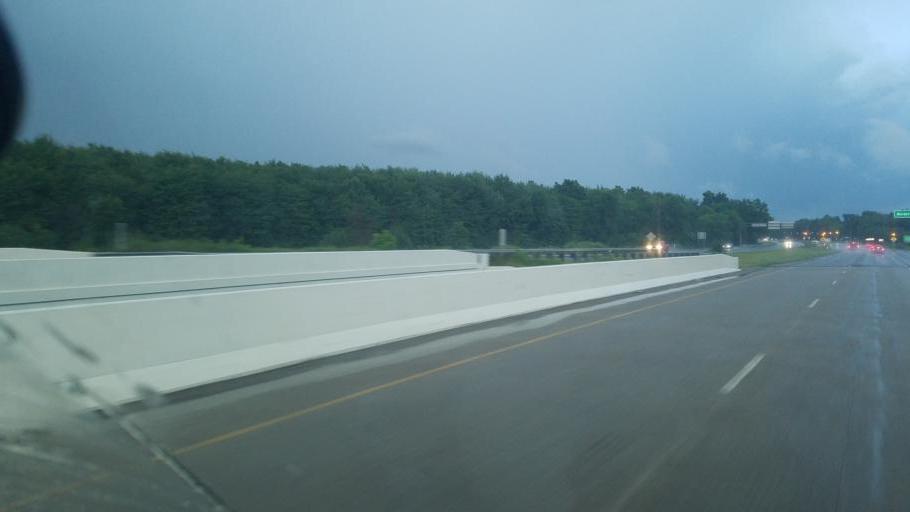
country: US
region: Ohio
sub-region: Wayne County
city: Doylestown
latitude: 40.9930
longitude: -81.6630
